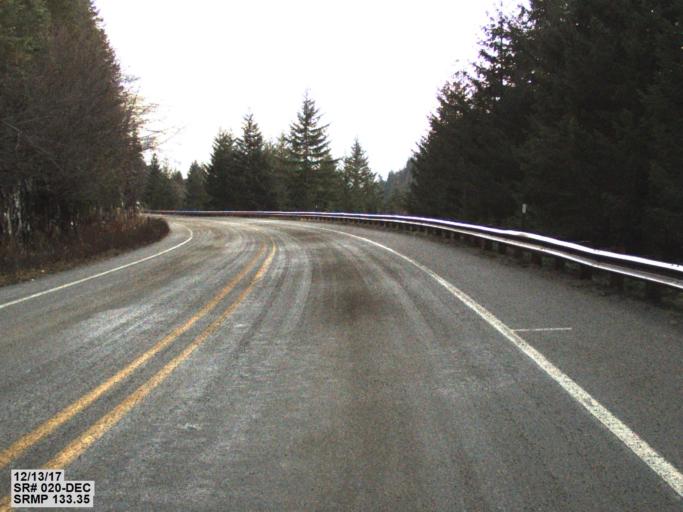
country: US
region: Washington
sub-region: Snohomish County
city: Darrington
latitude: 48.7188
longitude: -121.0712
